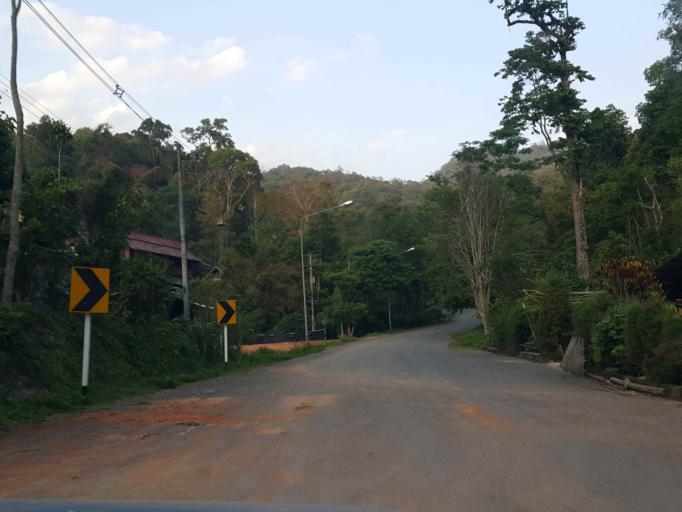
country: TH
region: Chiang Mai
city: Mae On
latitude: 18.9918
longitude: 99.3435
